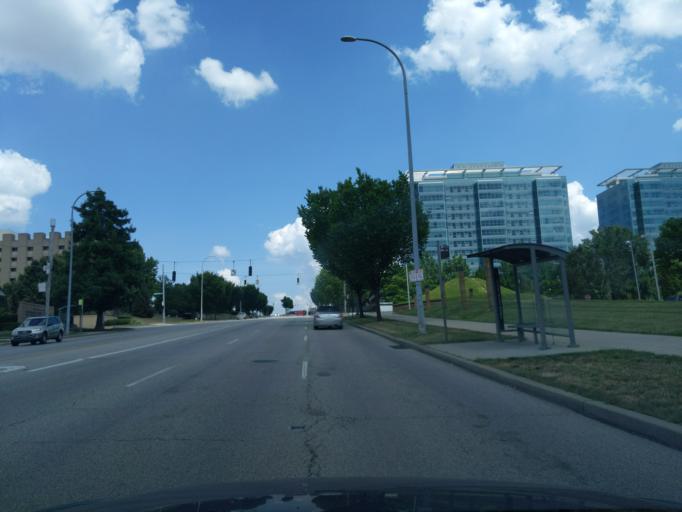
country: US
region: Ohio
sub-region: Hamilton County
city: Saint Bernard
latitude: 39.1356
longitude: -84.5139
